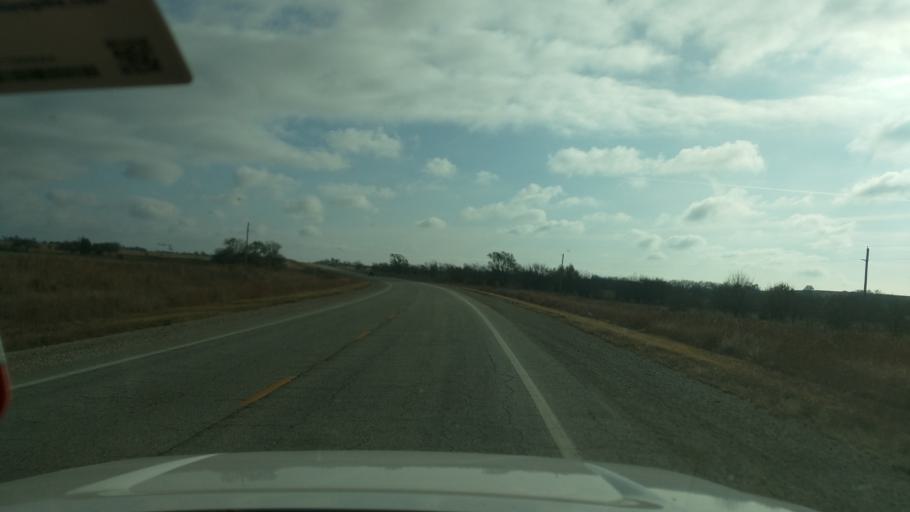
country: US
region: Kansas
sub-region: Chautauqua County
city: Sedan
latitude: 37.0839
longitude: -96.2163
